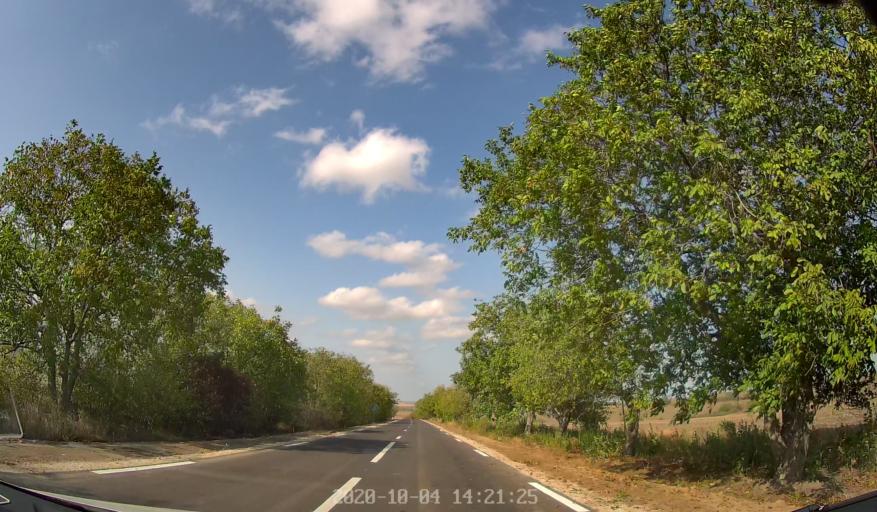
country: MD
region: Rezina
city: Saharna
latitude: 47.5848
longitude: 28.9557
